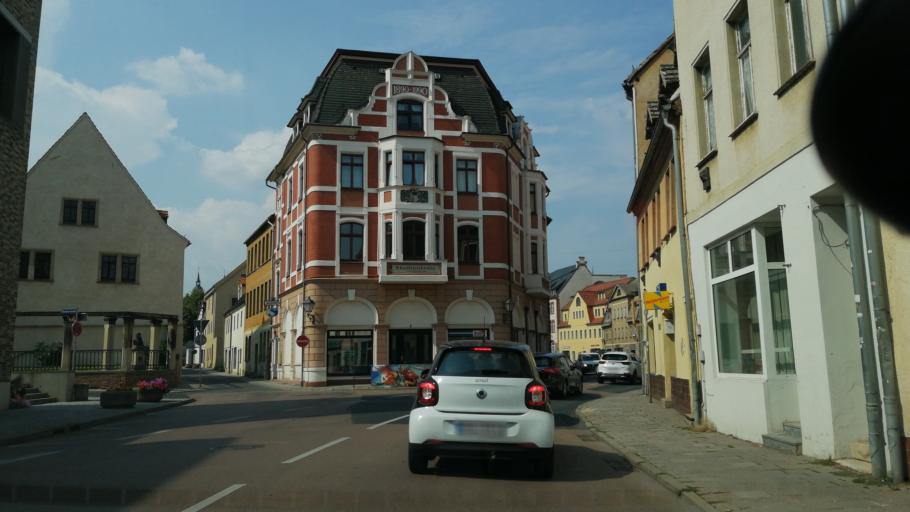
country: DE
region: Saxony-Anhalt
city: Wimmelburg
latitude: 51.5268
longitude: 11.5508
